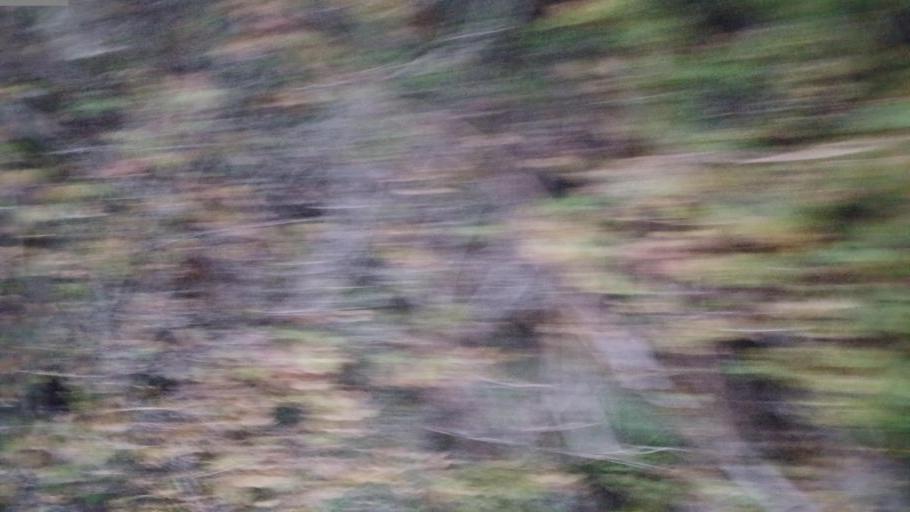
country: CY
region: Pafos
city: Mesogi
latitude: 34.8572
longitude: 32.5040
